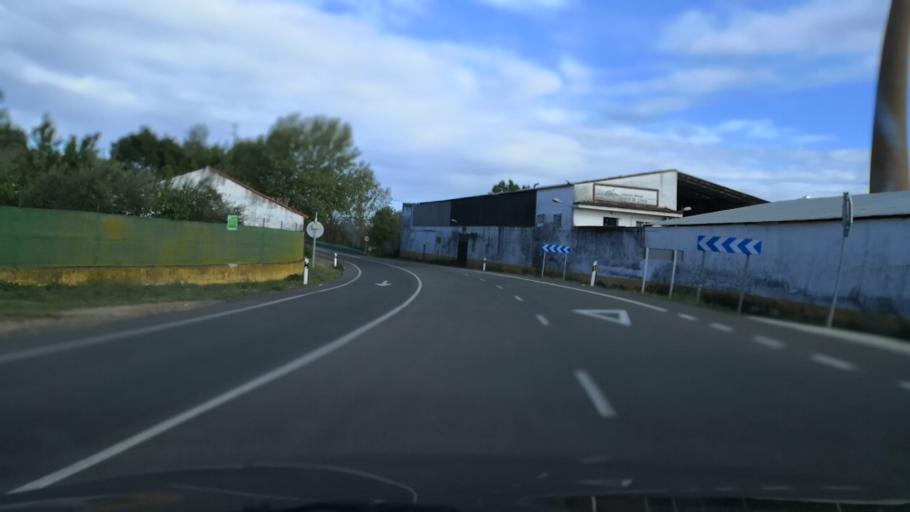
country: ES
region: Extremadura
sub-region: Provincia de Caceres
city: Moraleja
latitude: 40.0770
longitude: -6.6680
